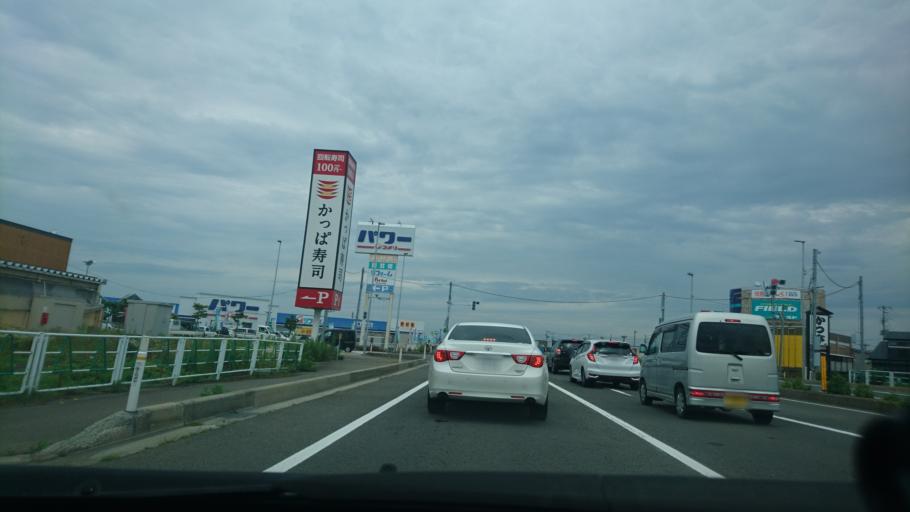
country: JP
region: Akita
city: Omagari
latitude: 39.4699
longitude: 140.4860
